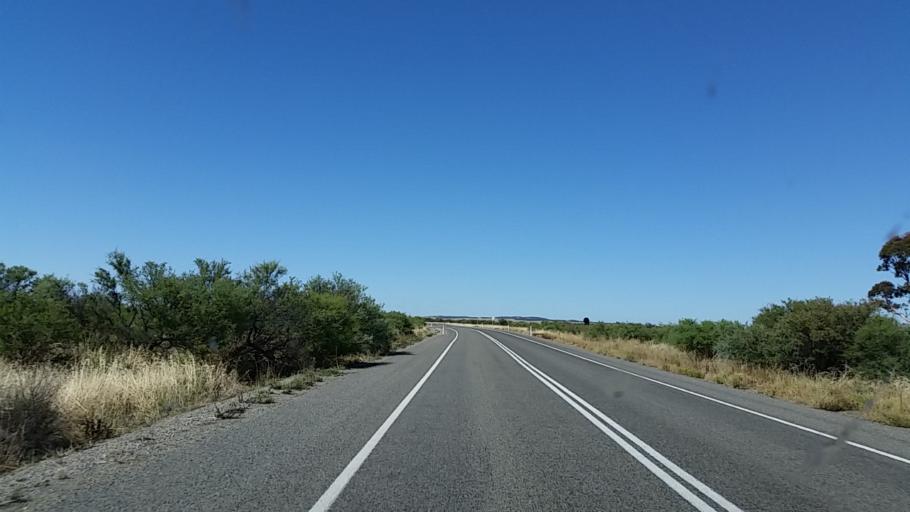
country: AU
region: South Australia
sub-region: Peterborough
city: Peterborough
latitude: -33.1714
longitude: 138.9114
